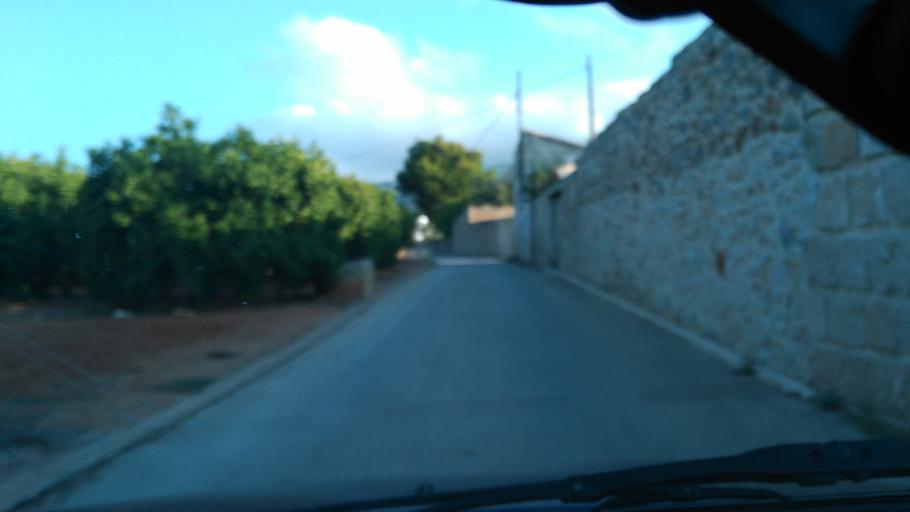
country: ES
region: Valencia
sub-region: Provincia de Alicante
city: Gata de Gorgos
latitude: 38.7836
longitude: 0.0894
